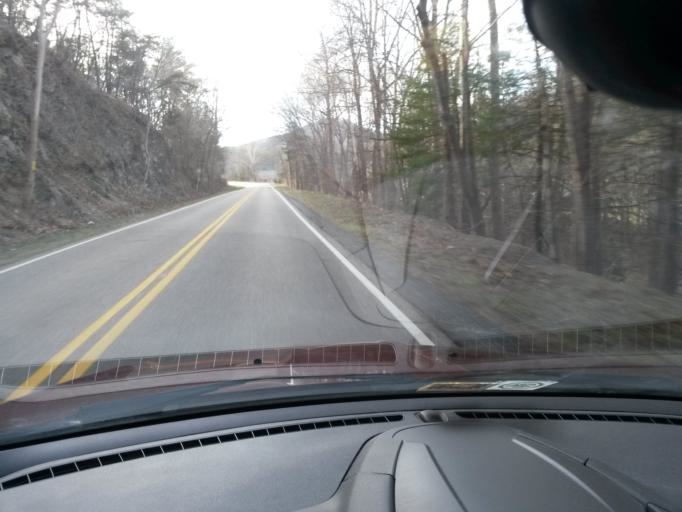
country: US
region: Virginia
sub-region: Alleghany County
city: Clifton Forge
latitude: 37.8959
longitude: -79.7466
